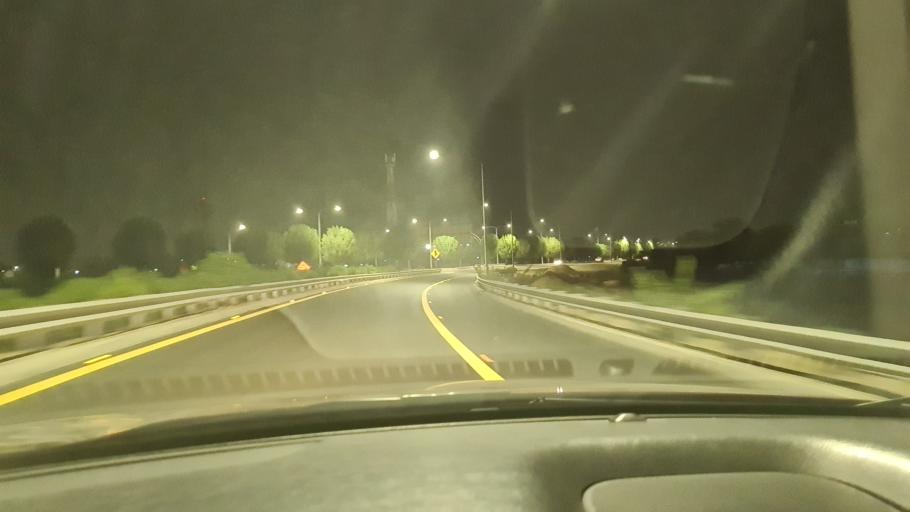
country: SA
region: Eastern Province
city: Al Jubayl
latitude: 27.1226
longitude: 49.5420
